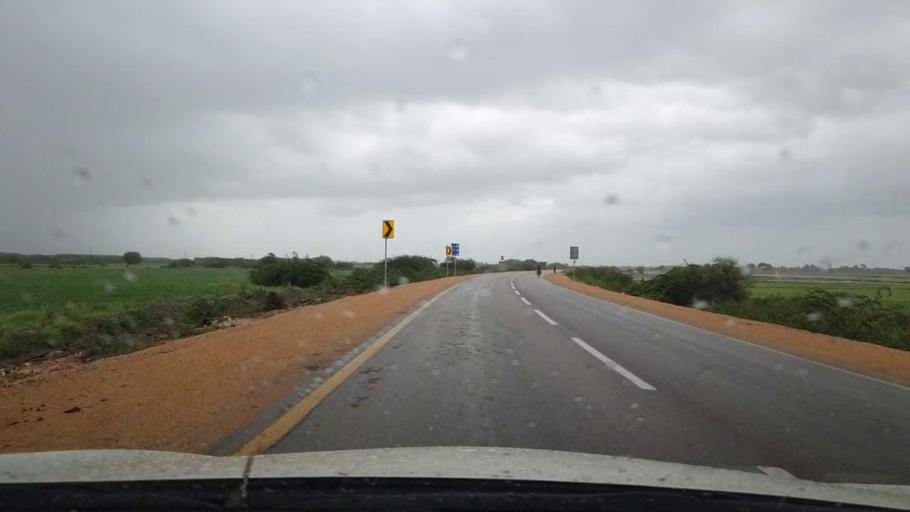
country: PK
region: Sindh
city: Badin
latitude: 24.6562
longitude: 68.6813
